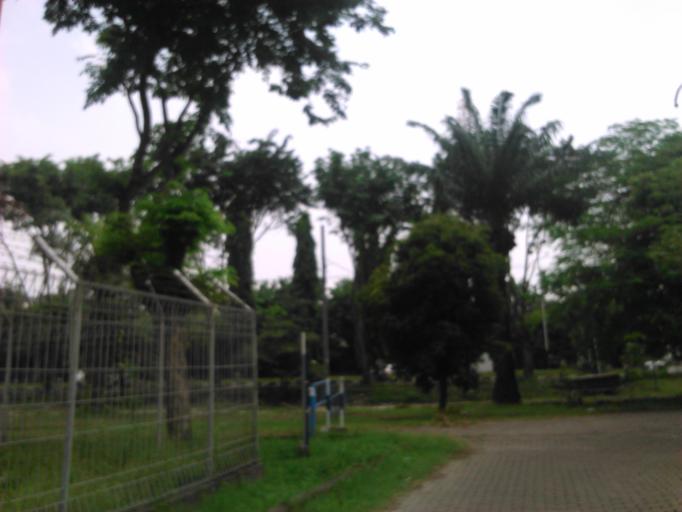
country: ID
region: East Java
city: Mulyorejo
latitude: -7.2765
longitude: 112.7927
